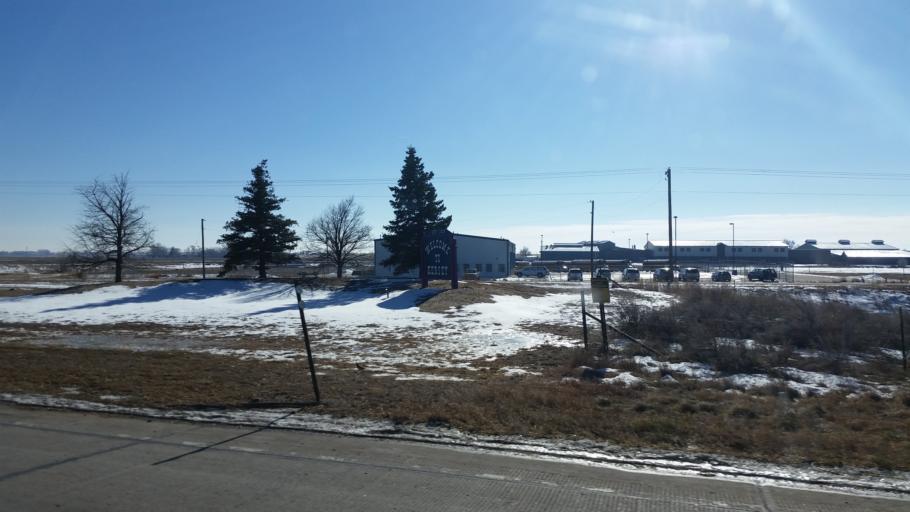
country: US
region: Colorado
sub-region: Weld County
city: Kersey
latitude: 40.3927
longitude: -104.5515
